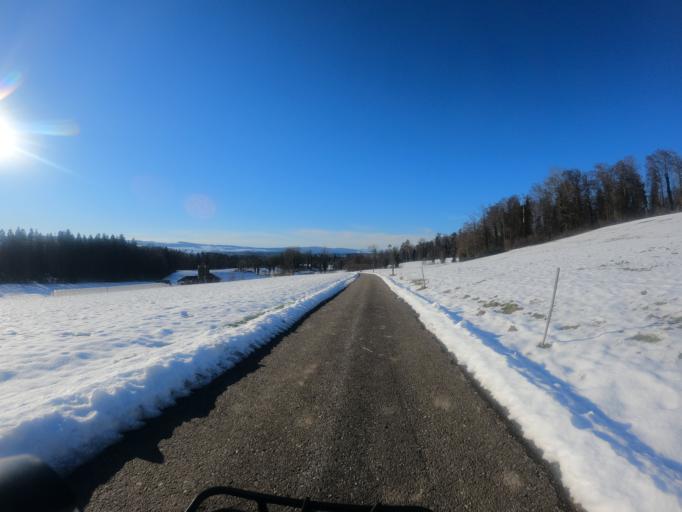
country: CH
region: Aargau
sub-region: Bezirk Bremgarten
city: Oberlunkhofen
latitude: 47.3202
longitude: 8.4027
